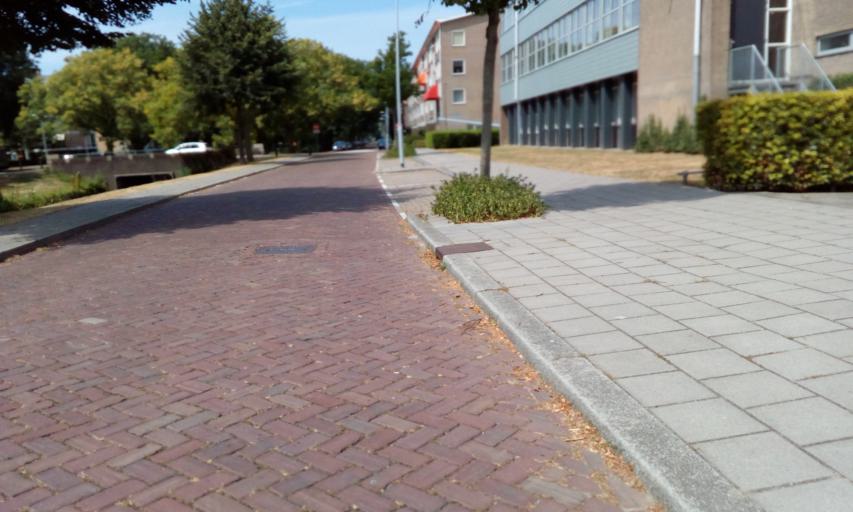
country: NL
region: South Holland
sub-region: Gemeente Leidschendam-Voorburg
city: Voorburg
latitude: 52.0729
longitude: 4.3563
